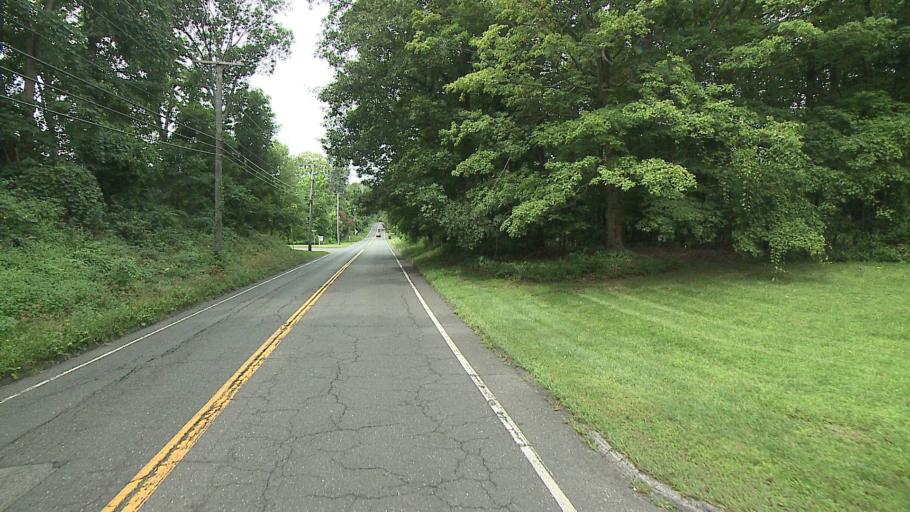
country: US
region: Connecticut
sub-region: Fairfield County
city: Newtown
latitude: 41.4694
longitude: -73.3732
